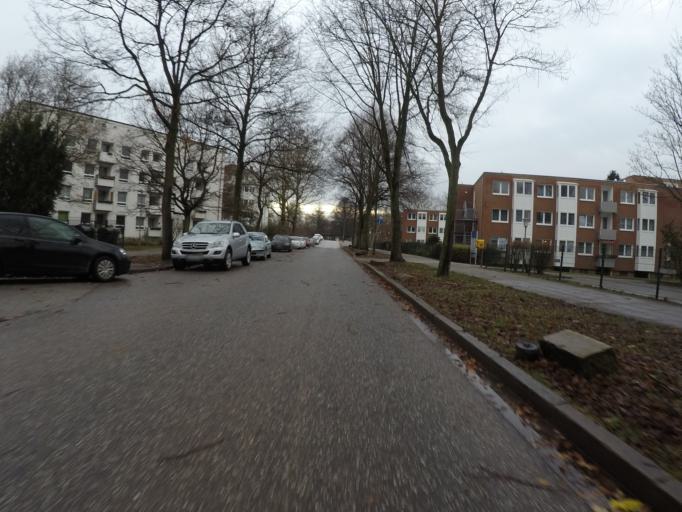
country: DE
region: Hamburg
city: Kleiner Grasbrook
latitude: 53.5055
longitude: 9.9950
